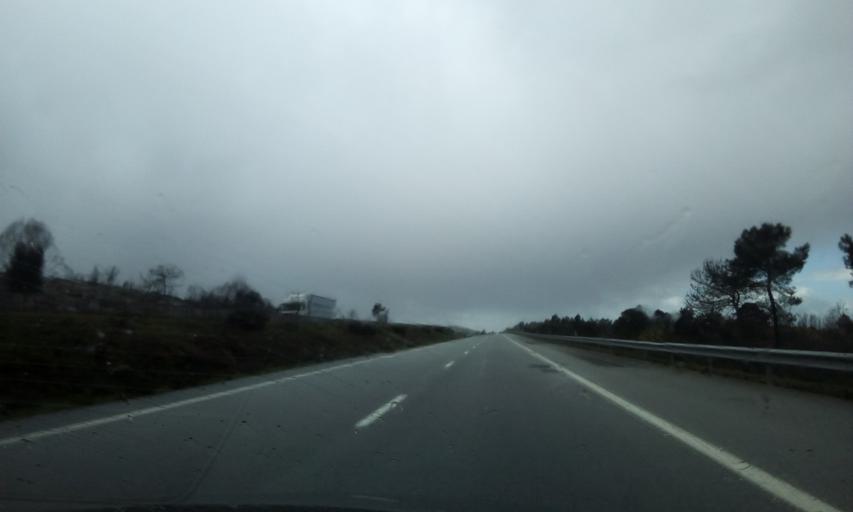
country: PT
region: Viseu
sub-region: Mangualde
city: Mangualde
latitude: 40.6137
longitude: -7.6978
